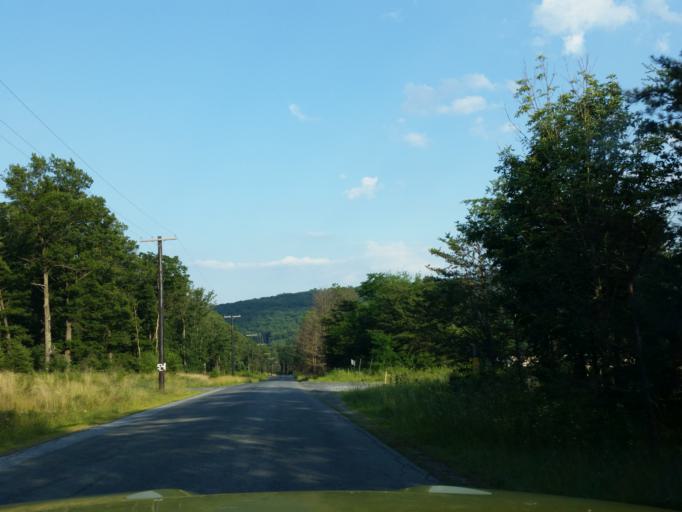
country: US
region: Pennsylvania
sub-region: Dauphin County
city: Williamstown
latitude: 40.4513
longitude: -76.6259
